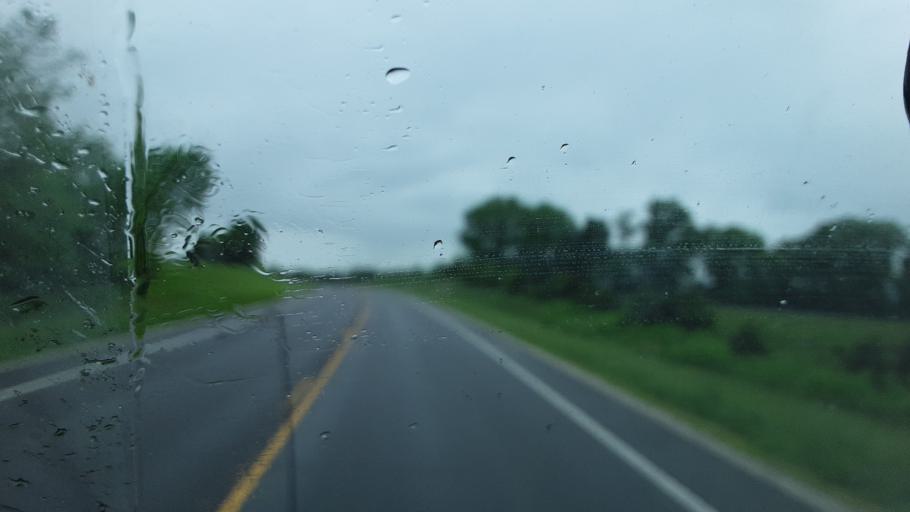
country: US
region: Missouri
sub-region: Monroe County
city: Paris
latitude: 39.4814
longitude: -92.1228
